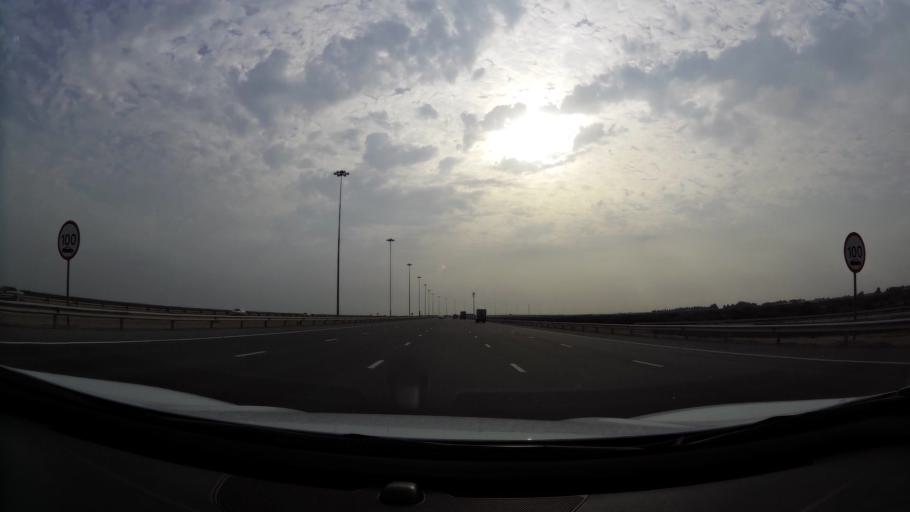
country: AE
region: Abu Dhabi
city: Abu Dhabi
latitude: 24.5472
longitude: 54.4689
